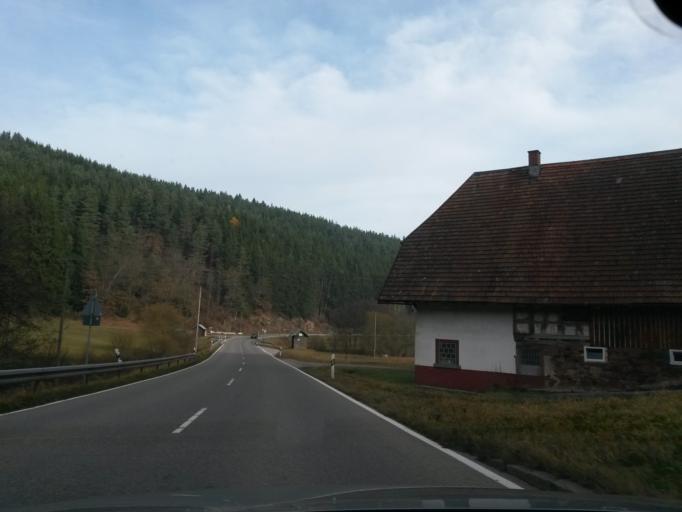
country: DE
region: Baden-Wuerttemberg
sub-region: Freiburg Region
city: Tennenbronn
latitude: 48.1743
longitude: 8.3288
